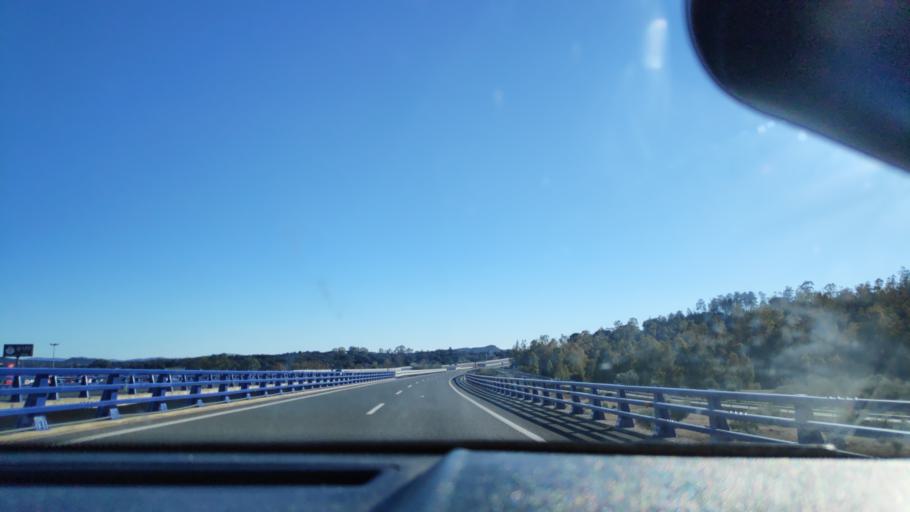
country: ES
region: Extremadura
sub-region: Provincia de Badajoz
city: Monesterio
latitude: 38.0305
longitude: -6.2225
